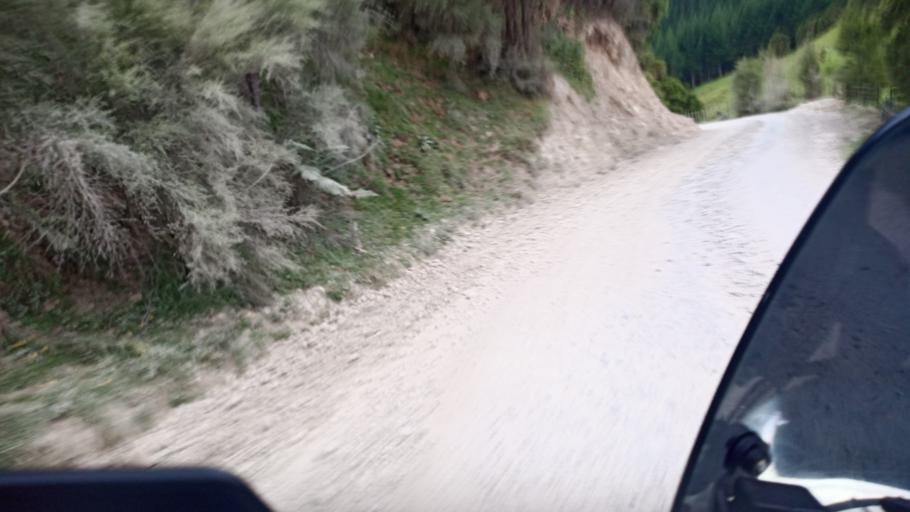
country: NZ
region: Gisborne
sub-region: Gisborne District
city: Gisborne
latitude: -38.4751
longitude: 177.9749
